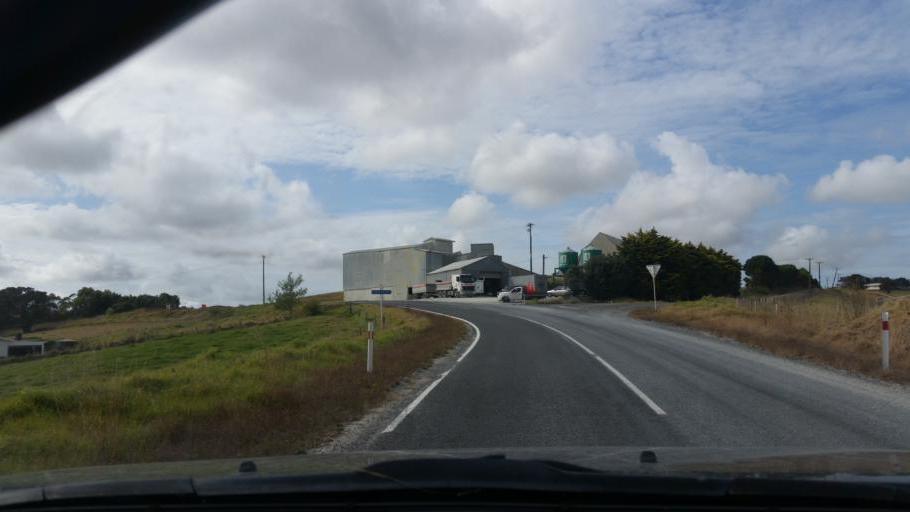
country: NZ
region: Northland
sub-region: Kaipara District
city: Dargaville
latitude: -35.9679
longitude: 173.9353
